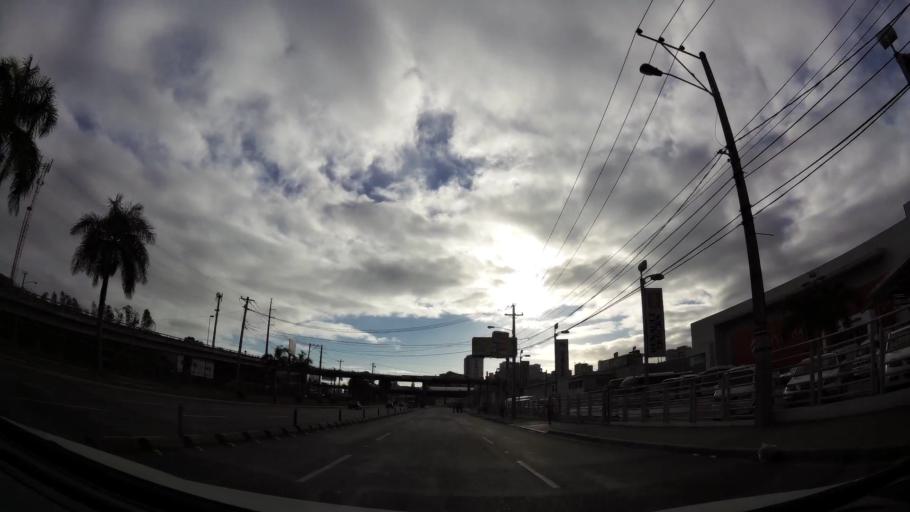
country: DO
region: Nacional
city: La Julia
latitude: 18.4820
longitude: -69.9481
